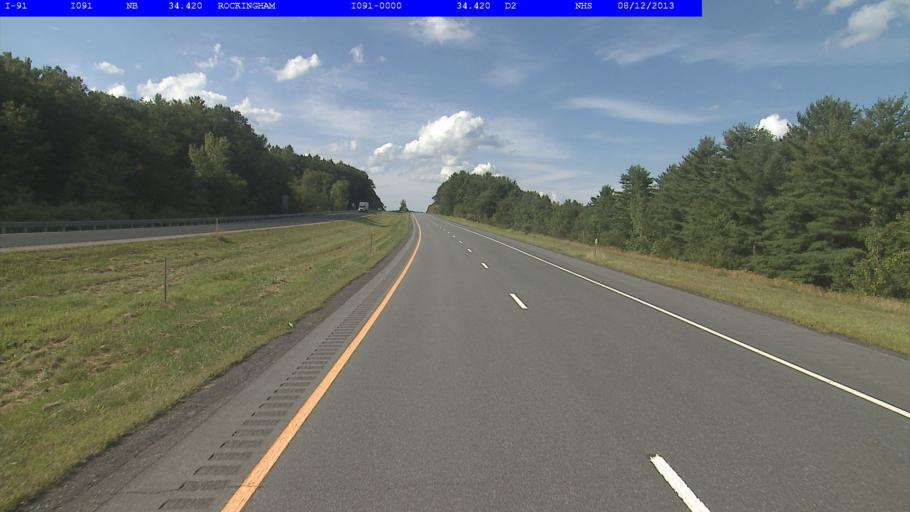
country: US
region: Vermont
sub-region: Windham County
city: Rockingham
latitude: 43.1674
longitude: -72.4620
